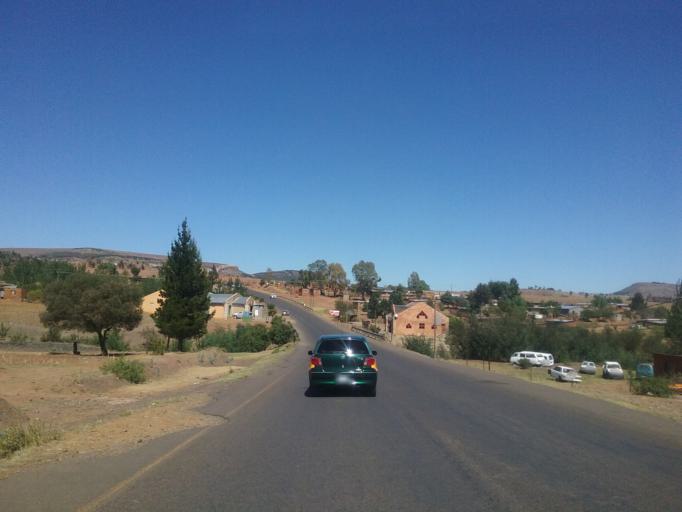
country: LS
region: Quthing
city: Quthing
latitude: -30.3975
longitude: 27.6630
